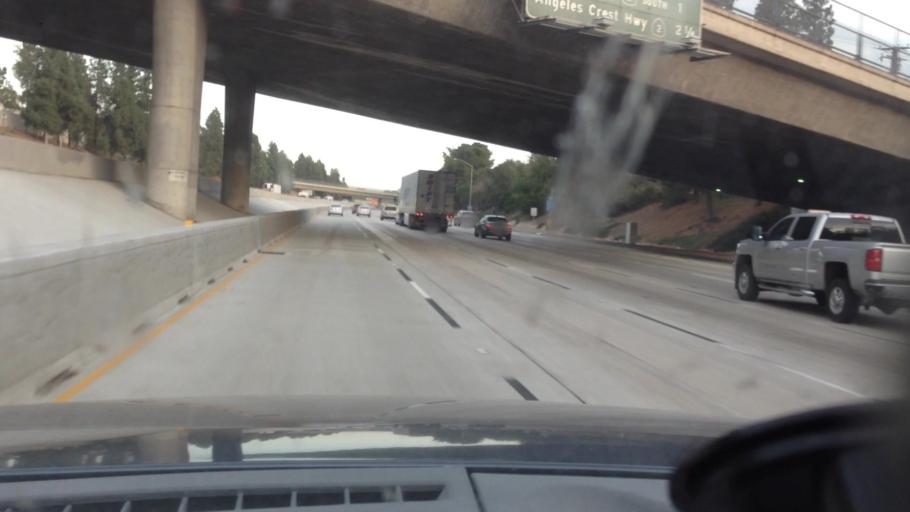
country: US
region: California
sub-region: Los Angeles County
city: La Crescenta-Montrose
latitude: 34.2189
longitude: -118.2405
